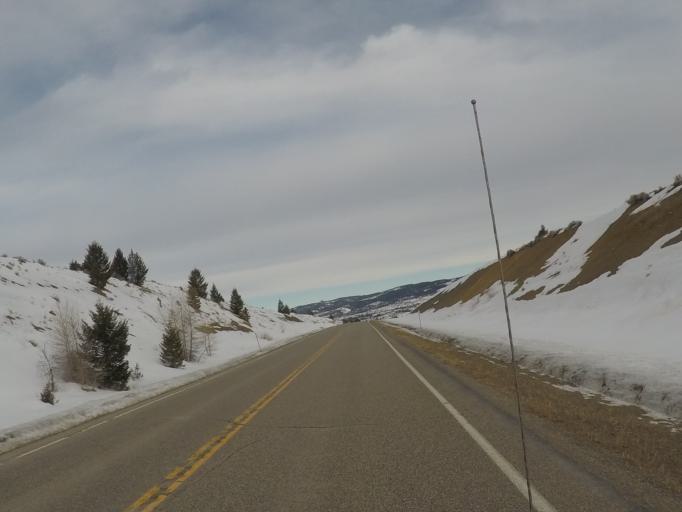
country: US
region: Montana
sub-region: Meagher County
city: White Sulphur Springs
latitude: 46.6451
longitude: -110.8662
